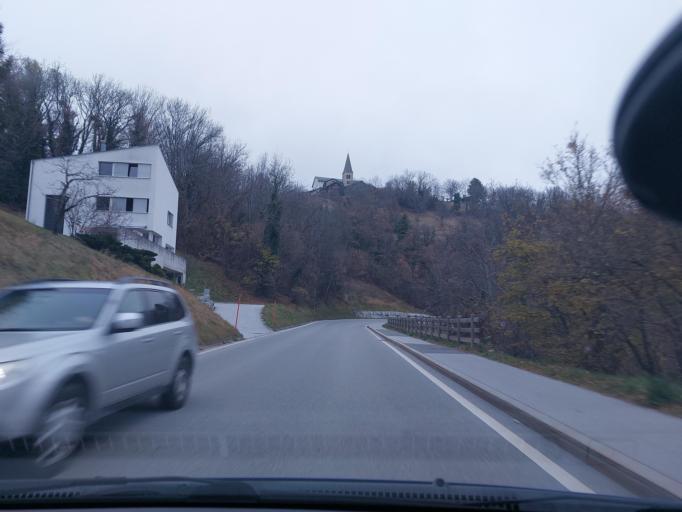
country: CH
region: Valais
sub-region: Herens District
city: Ayent
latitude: 46.2799
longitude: 7.4131
